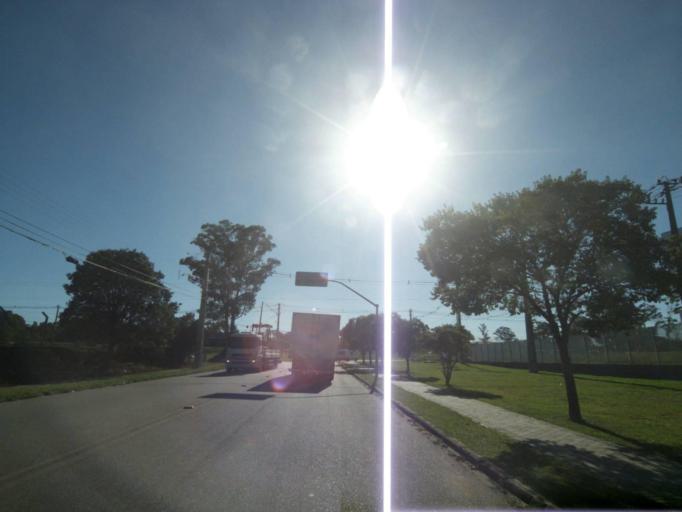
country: BR
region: Parana
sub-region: Curitiba
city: Curitiba
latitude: -25.4652
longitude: -49.3555
